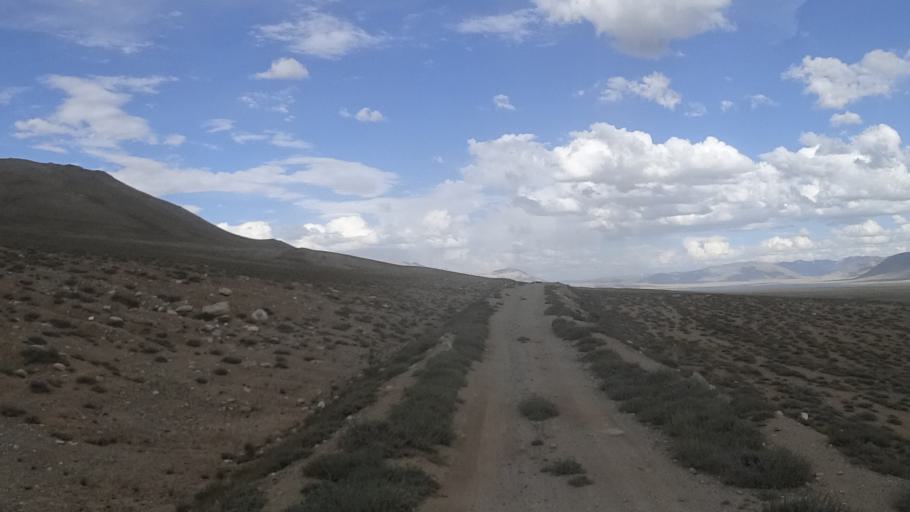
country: TJ
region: Gorno-Badakhshan
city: Murghob
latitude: 37.4685
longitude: 73.5766
